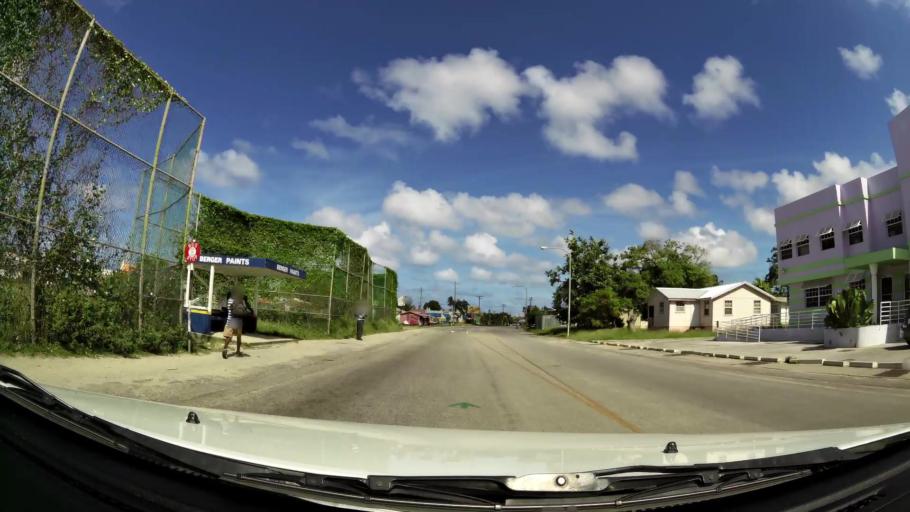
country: BB
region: Saint Peter
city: Speightstown
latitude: 13.2482
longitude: -59.6414
